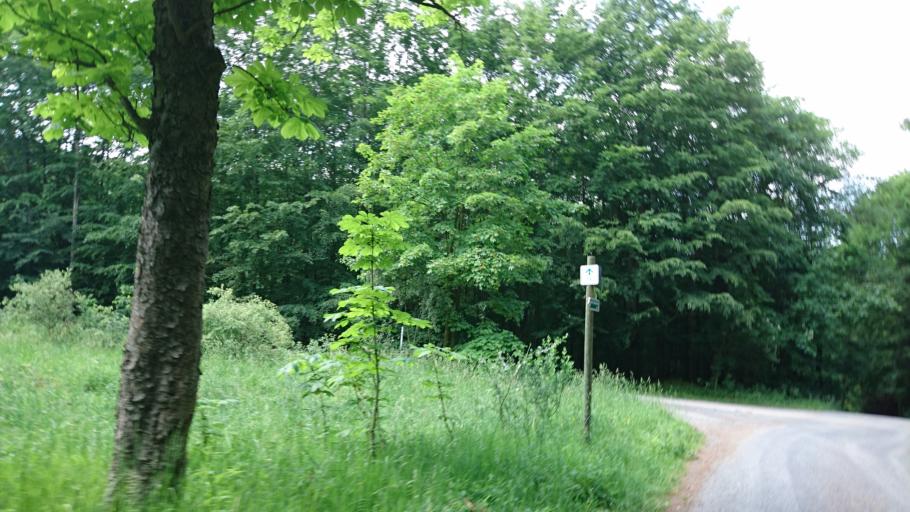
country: DE
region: Saxony
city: Bad Schandau
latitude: 50.8679
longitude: 14.1786
